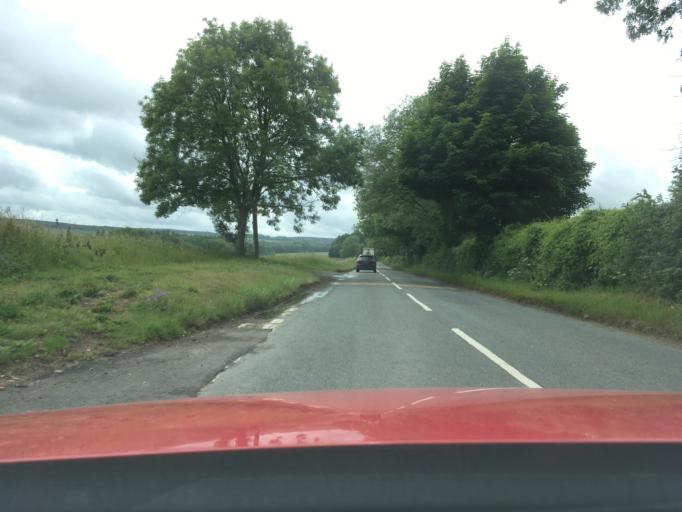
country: GB
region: England
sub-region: Gloucestershire
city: Chipping Campden
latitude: 52.0518
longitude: -1.8009
